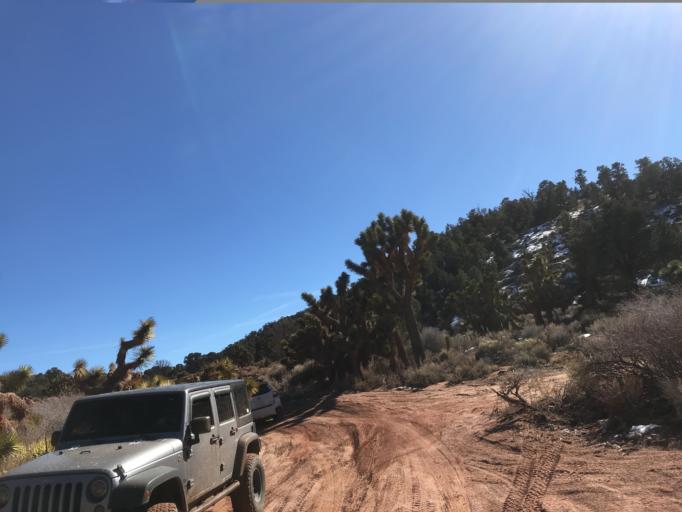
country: US
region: California
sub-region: San Bernardino County
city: Big Bear City
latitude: 34.2454
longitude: -116.7019
